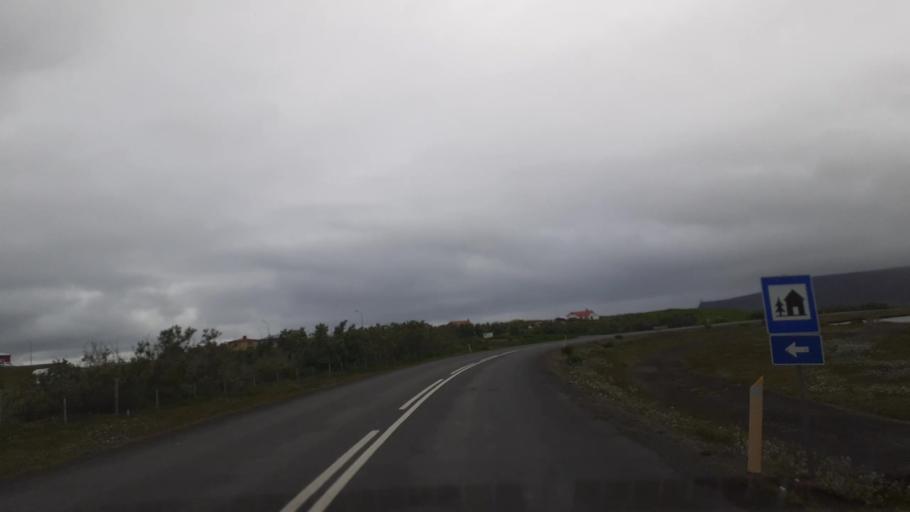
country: IS
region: Northeast
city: Husavik
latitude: 66.3004
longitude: -16.4389
